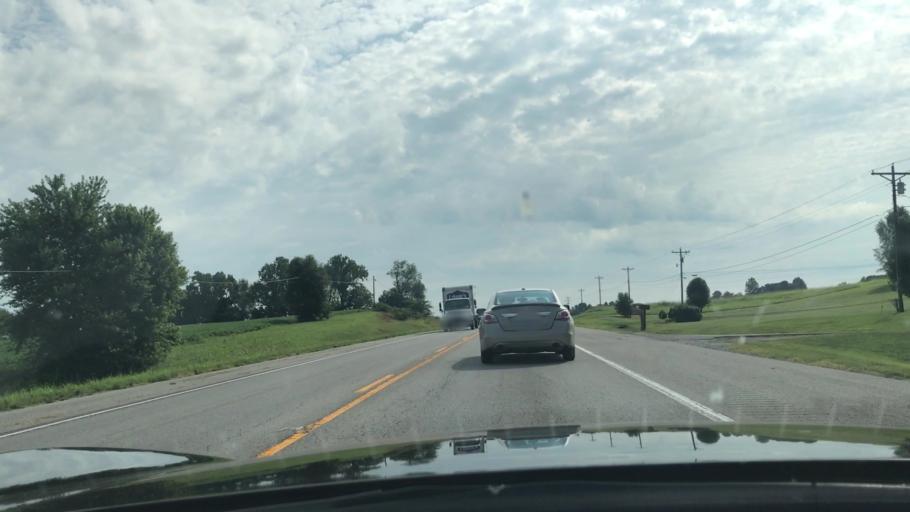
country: US
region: Kentucky
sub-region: Green County
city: Greensburg
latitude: 37.2963
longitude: -85.4612
